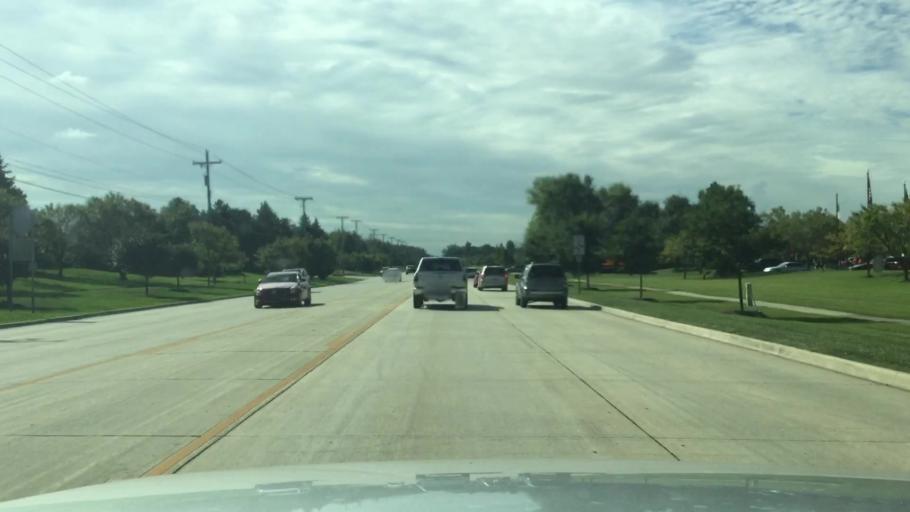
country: US
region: Michigan
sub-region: Wayne County
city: Canton
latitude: 42.2995
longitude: -83.4869
